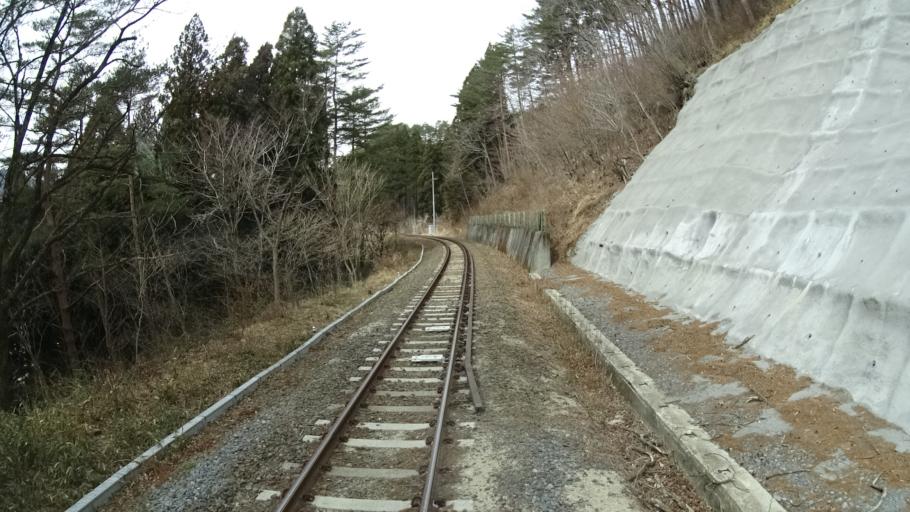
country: JP
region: Iwate
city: Yamada
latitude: 39.4756
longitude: 141.9294
